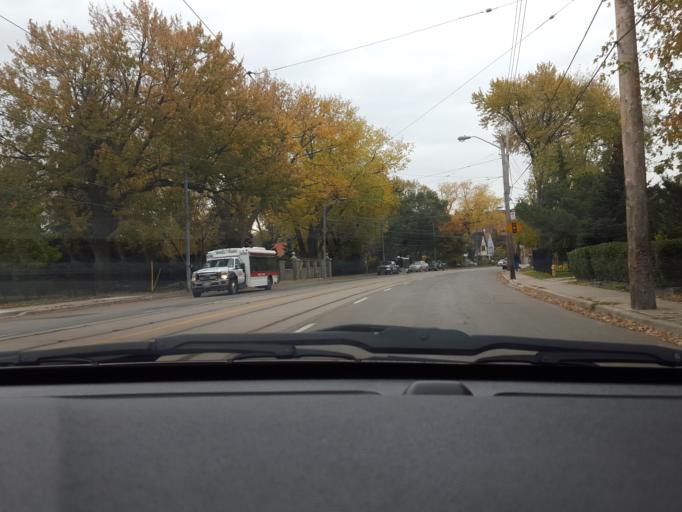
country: CA
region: Ontario
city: Etobicoke
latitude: 43.6050
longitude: -79.4915
